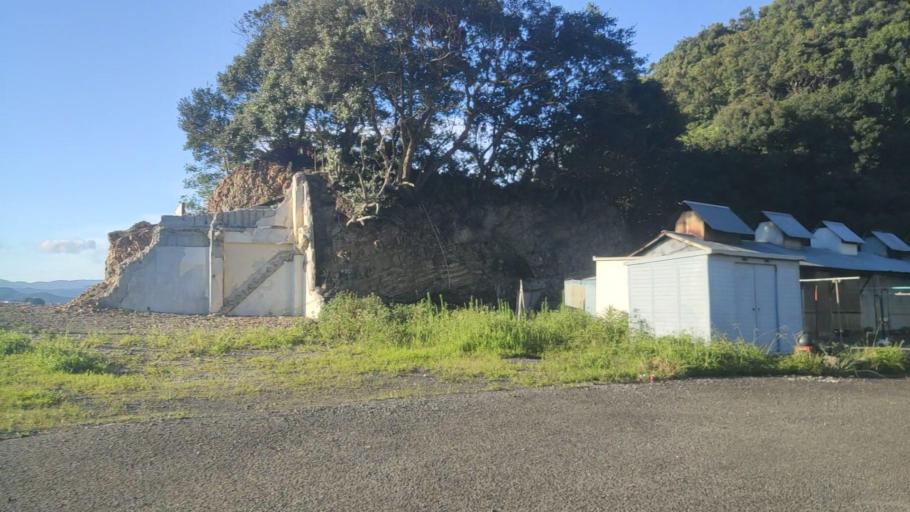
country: JP
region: Mie
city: Ise
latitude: 34.2781
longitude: 136.7699
